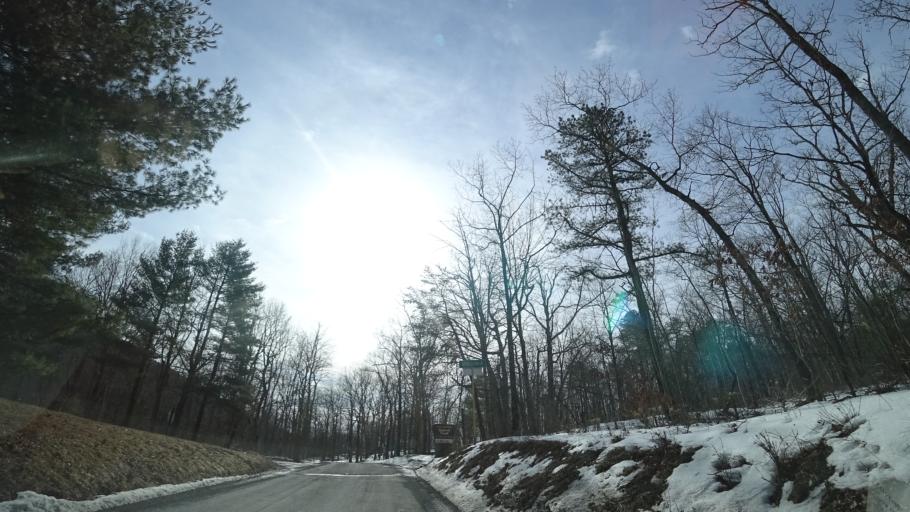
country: US
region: Virginia
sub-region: Shenandoah County
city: Basye
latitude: 38.9240
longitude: -78.6900
